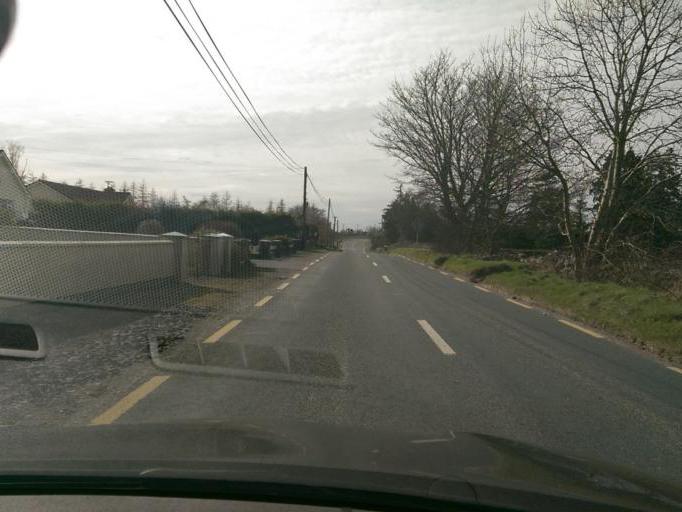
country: IE
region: Connaught
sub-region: County Galway
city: Tuam
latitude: 53.4291
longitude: -8.7611
